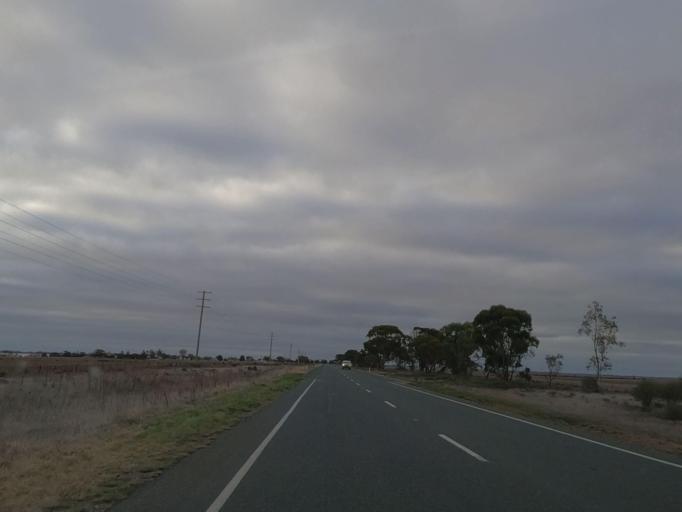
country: AU
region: Victoria
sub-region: Swan Hill
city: Swan Hill
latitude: -35.5910
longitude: 143.7905
